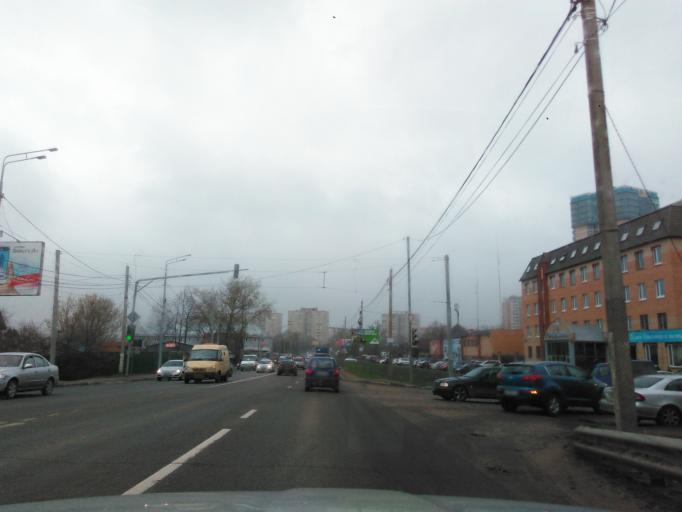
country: RU
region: Moskovskaya
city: Opalikha
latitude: 55.8351
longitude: 37.2853
